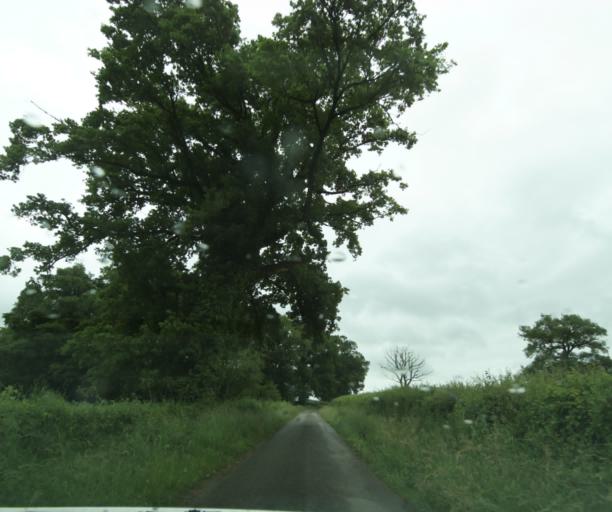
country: FR
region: Bourgogne
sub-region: Departement de Saone-et-Loire
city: Charolles
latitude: 46.4905
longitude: 4.2463
